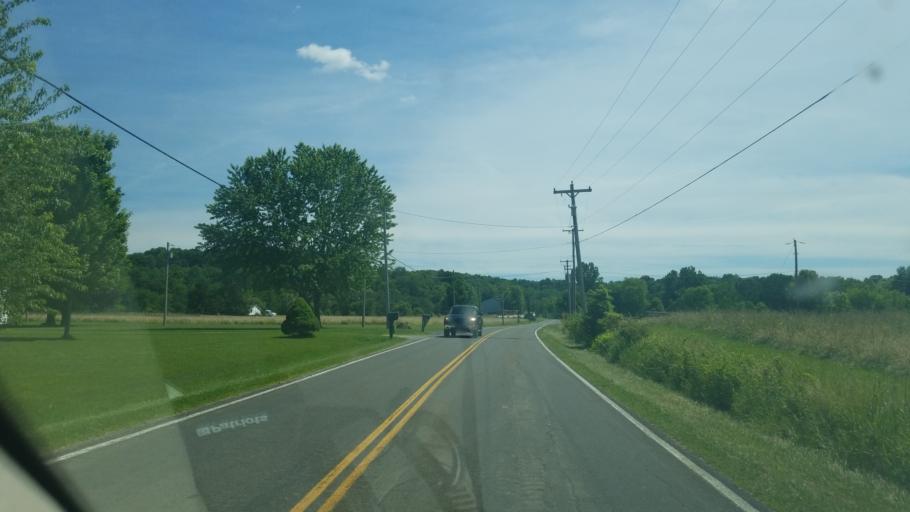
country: US
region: Ohio
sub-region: Stark County
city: Brewster
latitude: 40.7101
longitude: -81.5724
